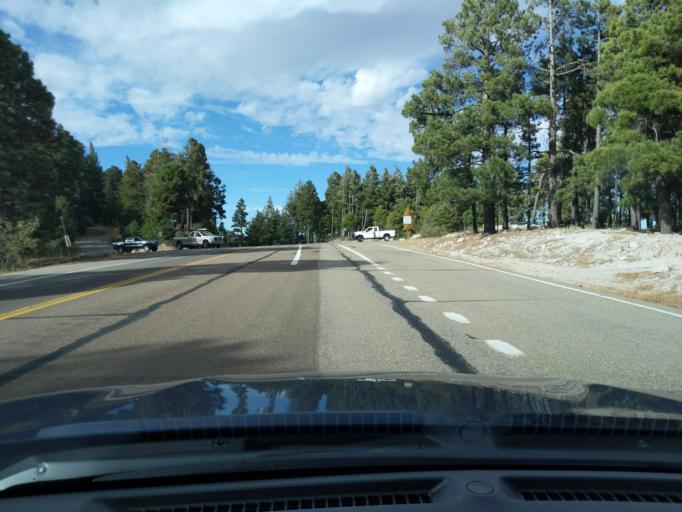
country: US
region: Arizona
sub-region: Pinal County
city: Oracle
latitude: 32.4397
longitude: -110.7524
